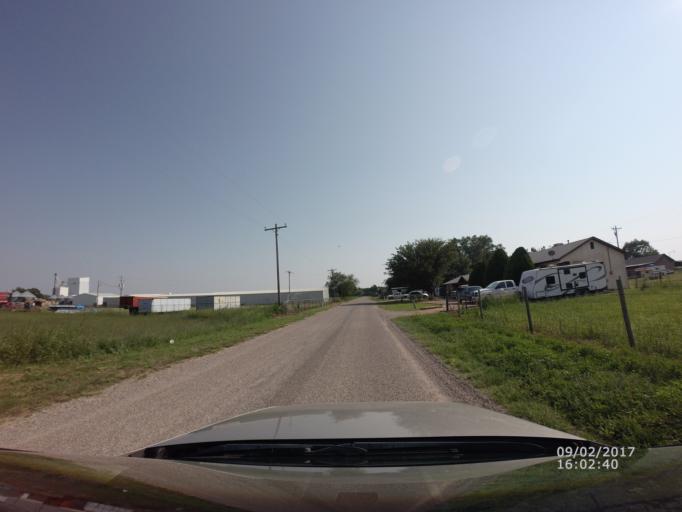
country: US
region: New Mexico
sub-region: Curry County
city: Clovis
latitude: 34.4449
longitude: -103.1996
